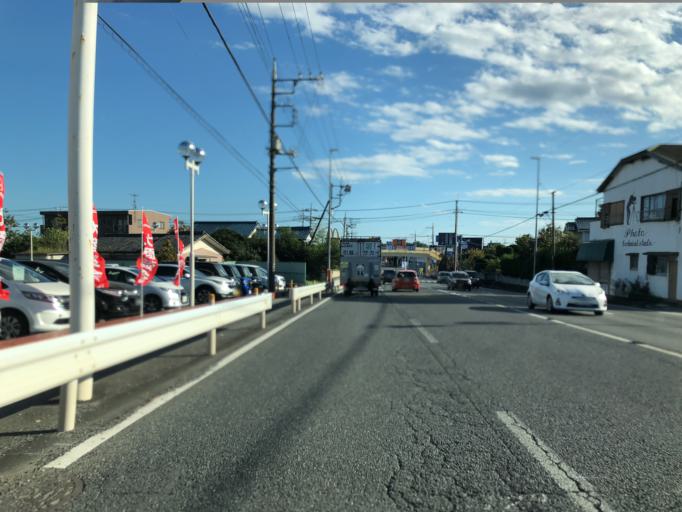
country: JP
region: Saitama
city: Fukiage-fujimi
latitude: 36.0386
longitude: 139.4162
